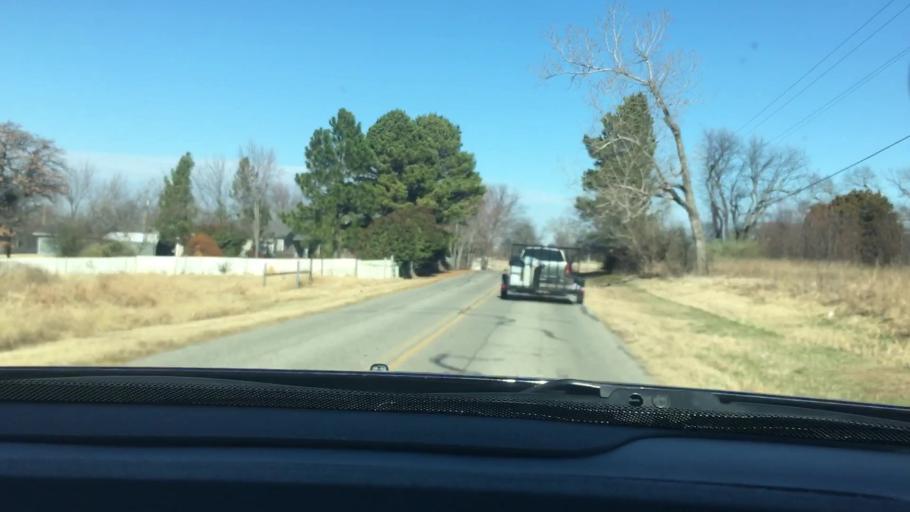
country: US
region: Oklahoma
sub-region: Murray County
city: Davis
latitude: 34.4781
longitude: -97.0556
